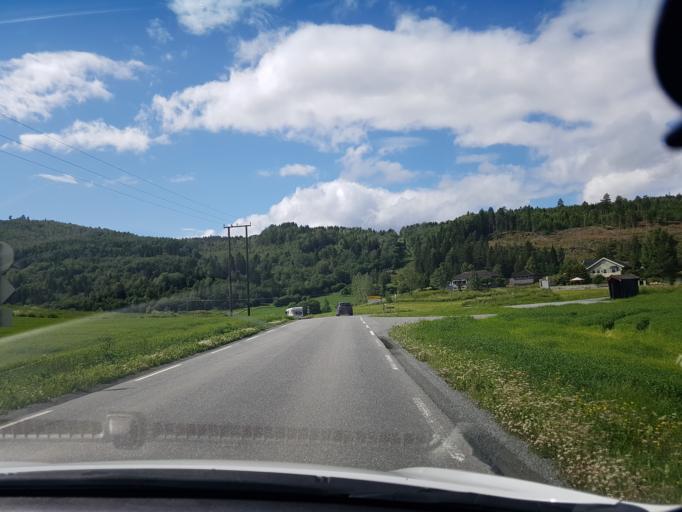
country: NO
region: Nord-Trondelag
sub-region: Frosta
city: Frosta
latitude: 63.5987
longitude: 10.8415
